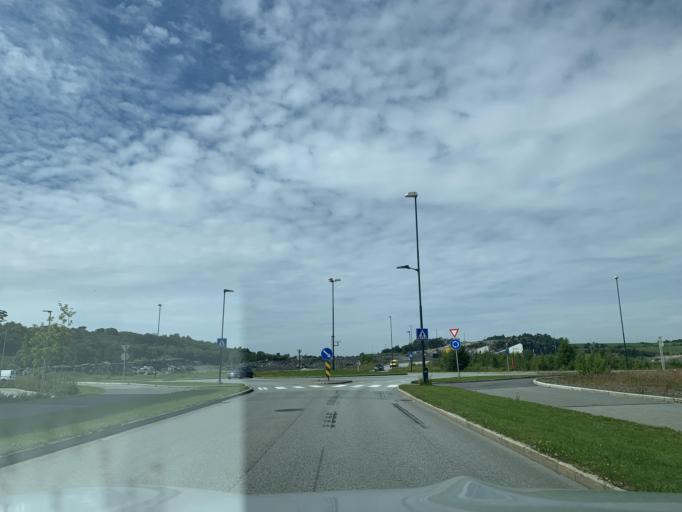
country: NO
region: Rogaland
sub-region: Sola
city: Sola
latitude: 58.8945
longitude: 5.6804
